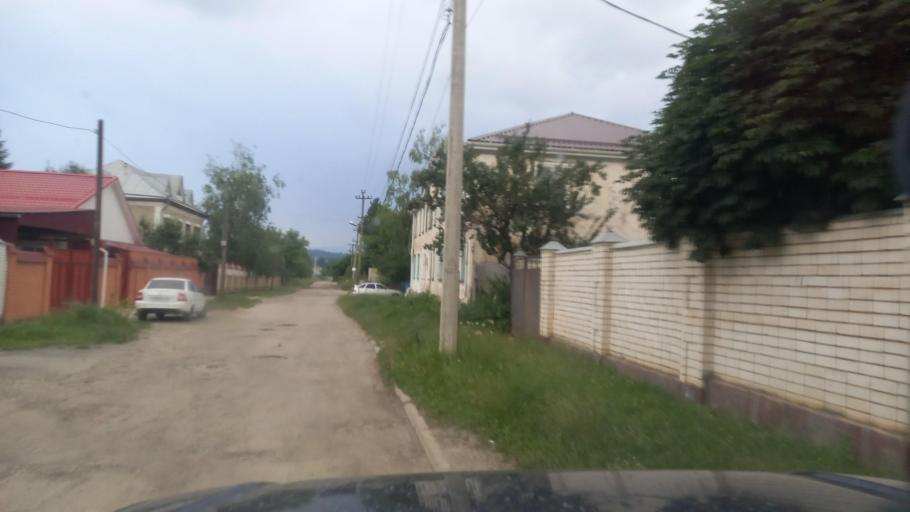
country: RU
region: Karachayevo-Cherkesiya
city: Pregradnaya
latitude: 43.9504
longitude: 41.1916
